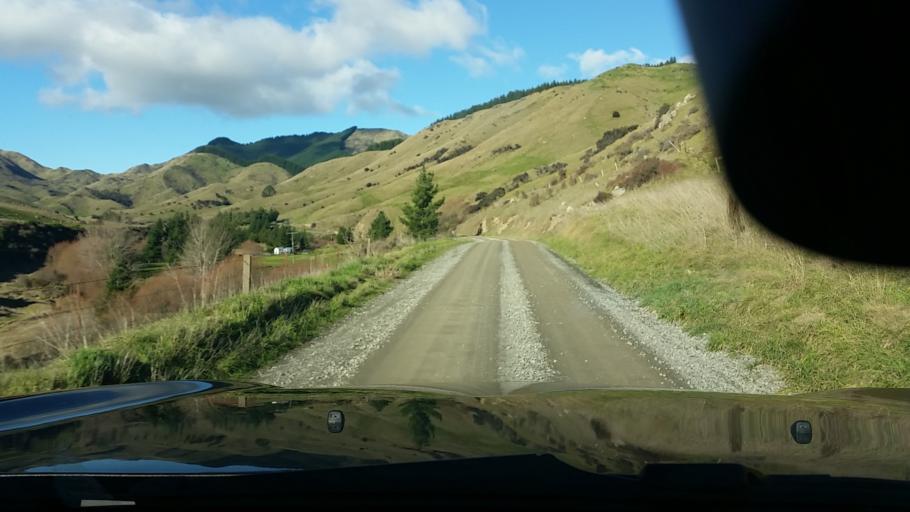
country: NZ
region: Marlborough
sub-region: Marlborough District
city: Blenheim
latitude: -41.6019
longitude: 173.9555
